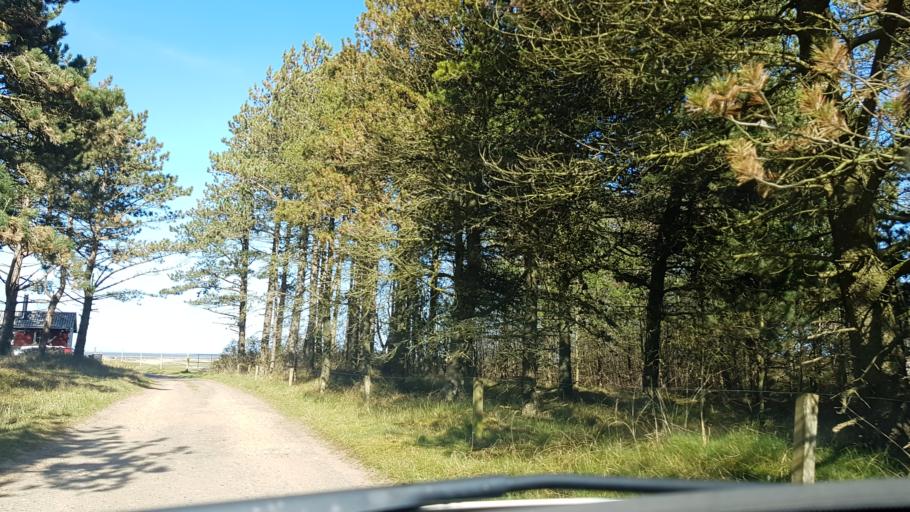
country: DE
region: Schleswig-Holstein
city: List
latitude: 55.0958
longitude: 8.5515
